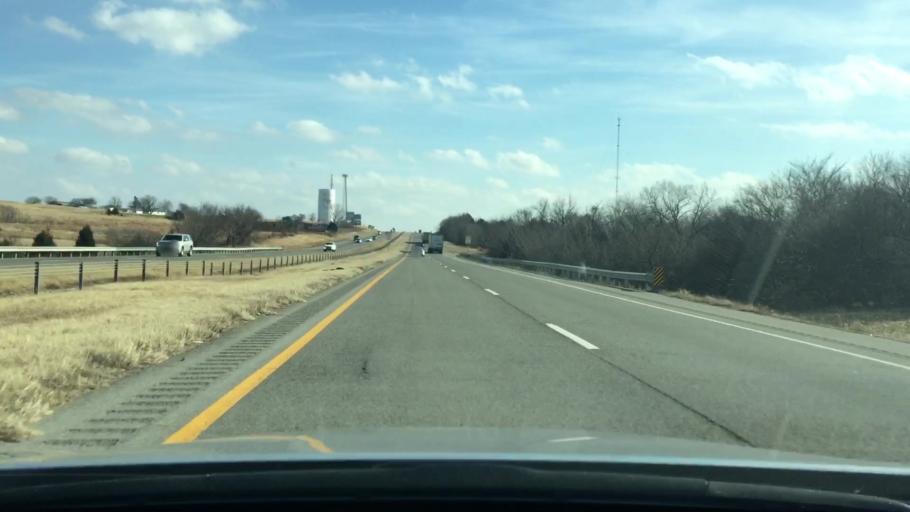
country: US
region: Oklahoma
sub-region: Cleveland County
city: Slaughterville
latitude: 35.0702
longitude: -97.3995
